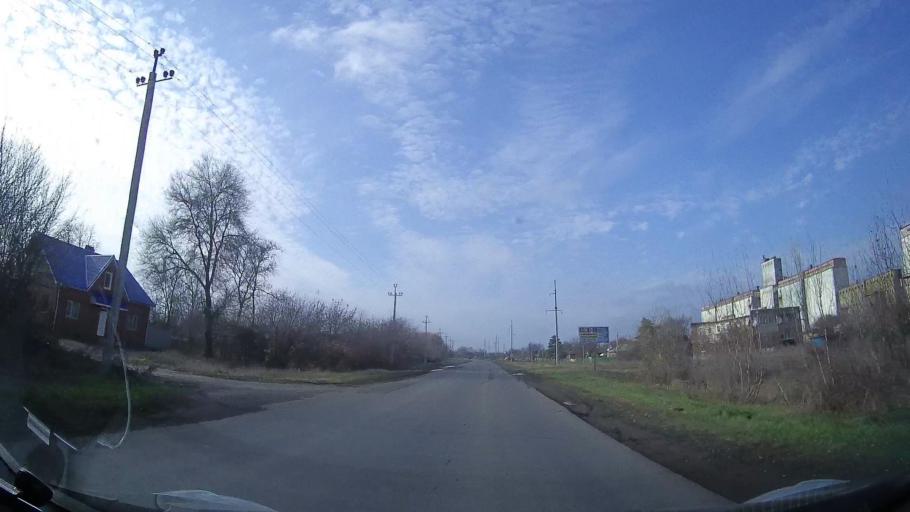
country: RU
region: Rostov
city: Mechetinskaya
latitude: 46.7861
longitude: 40.4797
